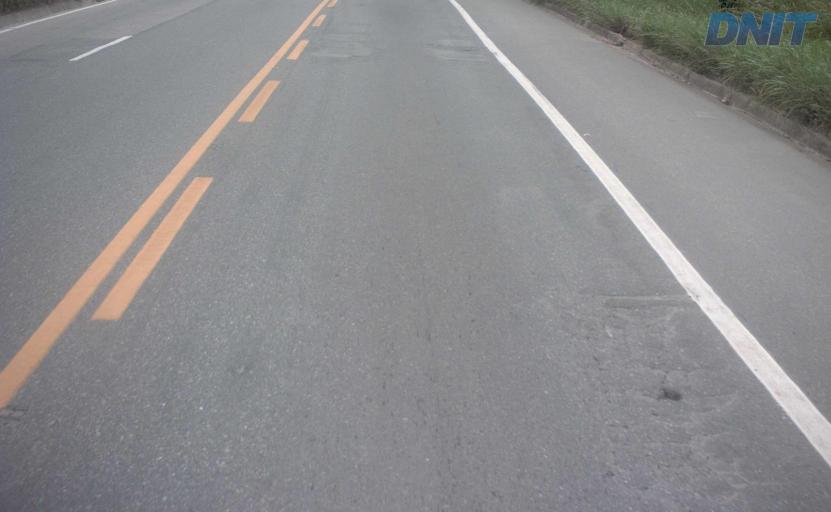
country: BR
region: Minas Gerais
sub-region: Nova Era
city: Nova Era
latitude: -19.7064
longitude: -42.9991
